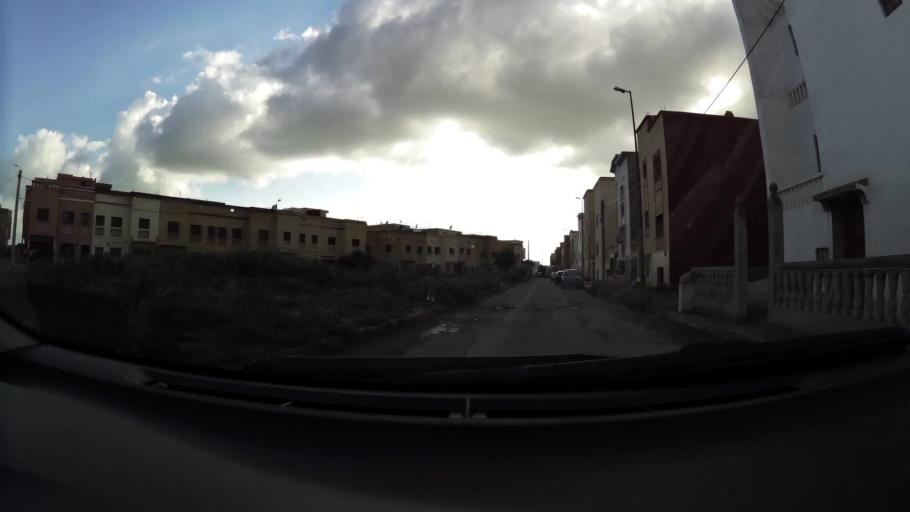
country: MA
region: Chaouia-Ouardigha
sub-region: Settat Province
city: Settat
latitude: 33.0052
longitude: -7.6429
